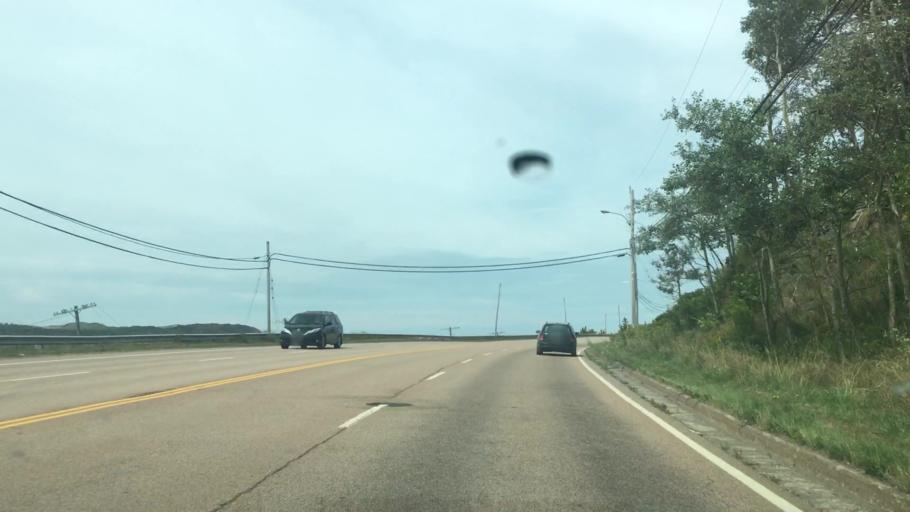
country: CA
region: Nova Scotia
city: Port Hawkesbury
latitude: 45.6264
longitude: -61.3715
